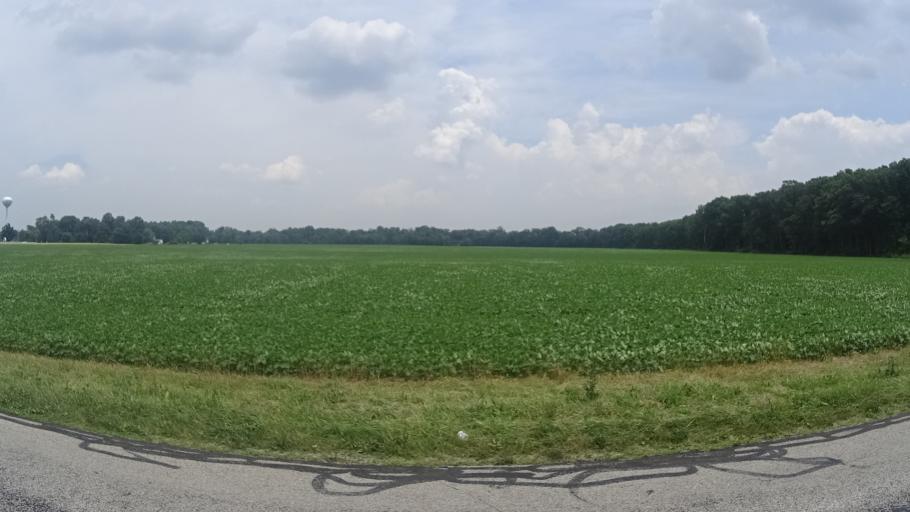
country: US
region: Ohio
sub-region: Erie County
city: Milan
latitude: 41.2932
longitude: -82.6467
